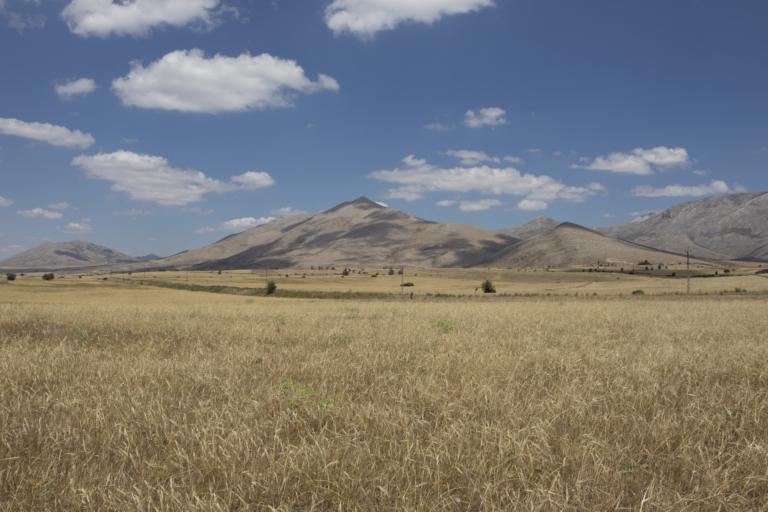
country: TR
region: Kayseri
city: Toklar
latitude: 38.4117
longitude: 36.0767
